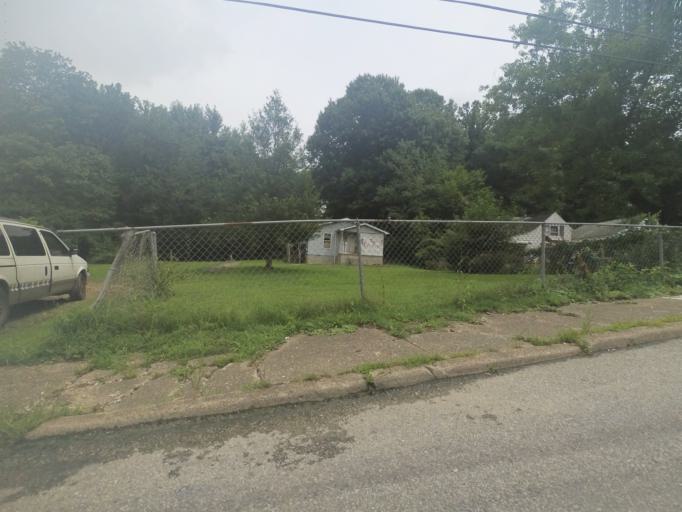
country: US
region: West Virginia
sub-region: Cabell County
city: Huntington
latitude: 38.4144
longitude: -82.4069
